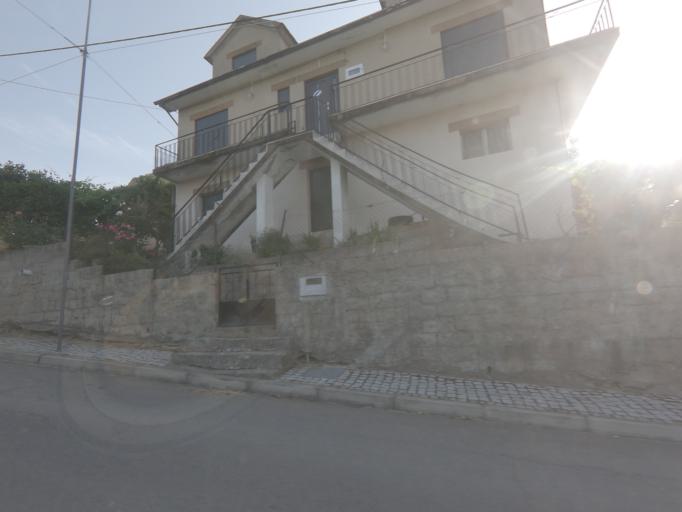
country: PT
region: Viseu
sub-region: Sao Joao da Pesqueira
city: Sao Joao da Pesqueira
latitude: 41.2281
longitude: -7.4679
